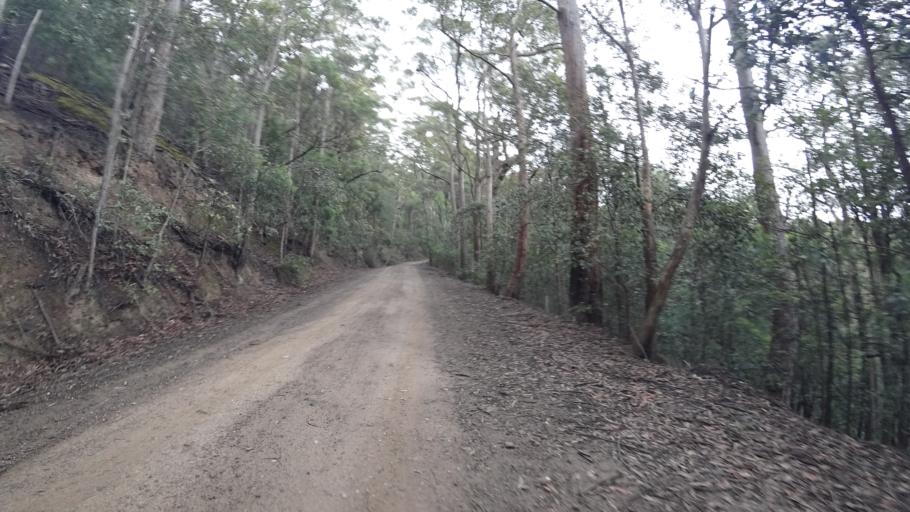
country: AU
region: New South Wales
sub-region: Shoalhaven Shire
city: Milton
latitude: -35.1730
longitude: 150.3742
